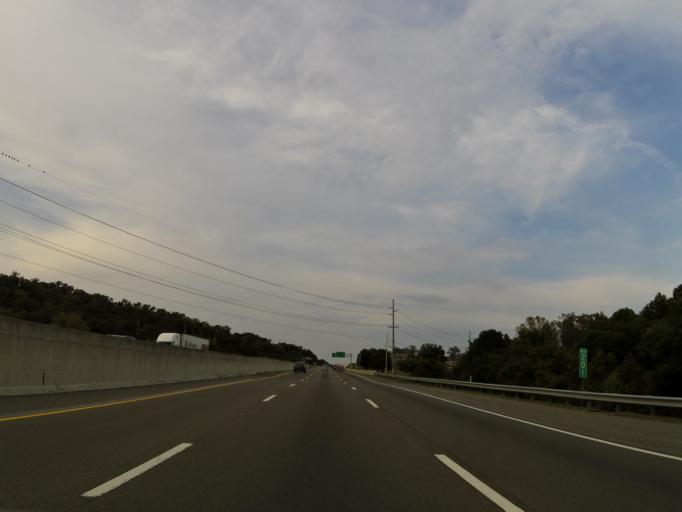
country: US
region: Tennessee
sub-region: Davidson County
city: Belle Meade
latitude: 36.1298
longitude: -86.8993
